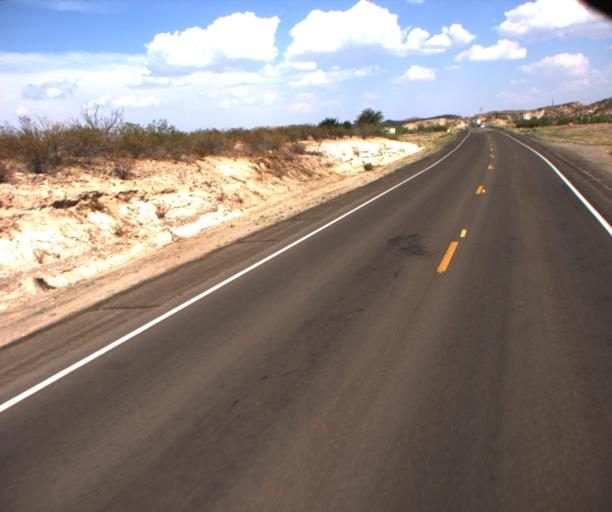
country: US
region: Arizona
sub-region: Greenlee County
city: Clifton
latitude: 32.7671
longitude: -109.1486
